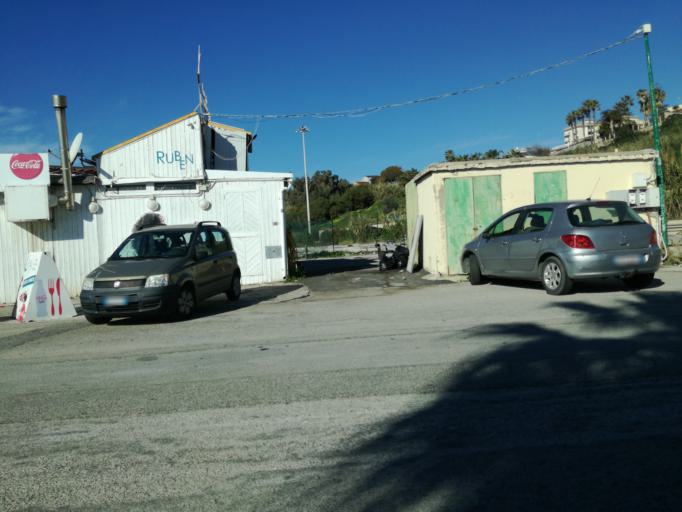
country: IT
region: Sicily
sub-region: Provincia di Caltanissetta
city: Gela
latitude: 37.0668
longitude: 14.2340
